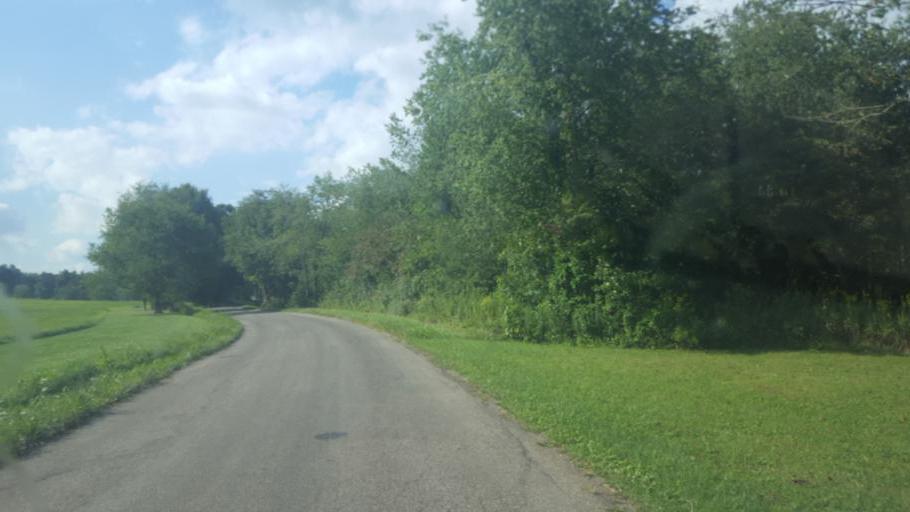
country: US
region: Ohio
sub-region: Knox County
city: Danville
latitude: 40.4863
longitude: -82.3122
